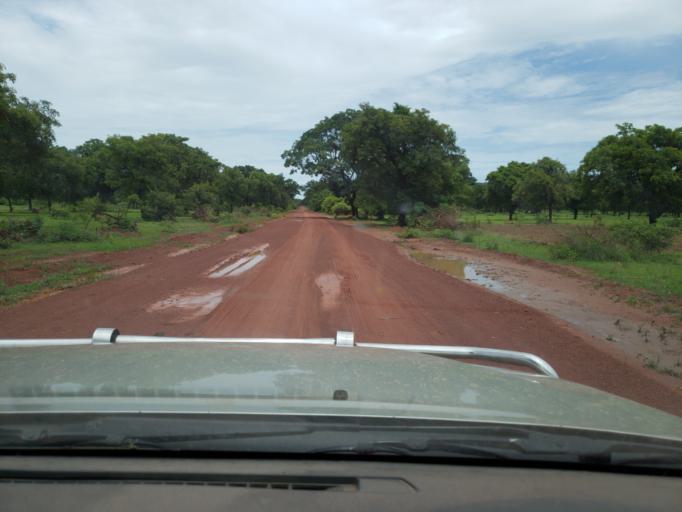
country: ML
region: Sikasso
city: Sikasso
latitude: 11.6667
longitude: -6.3421
